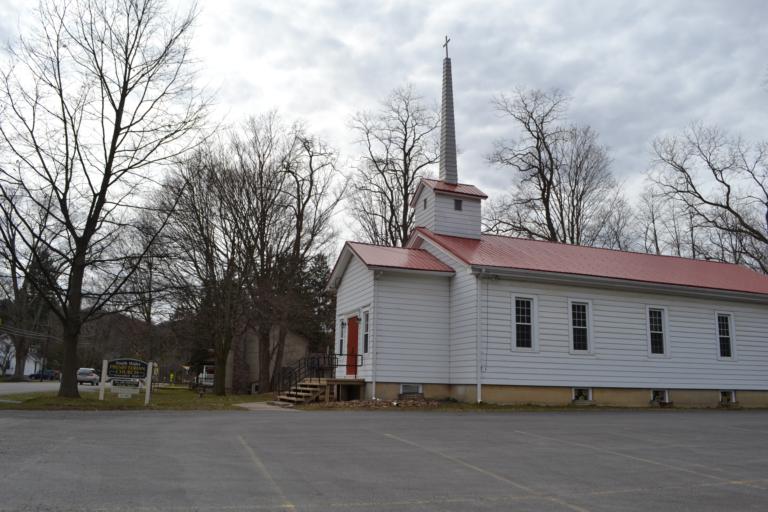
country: US
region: New York
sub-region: Erie County
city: East Aurora
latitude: 42.7093
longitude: -78.5793
